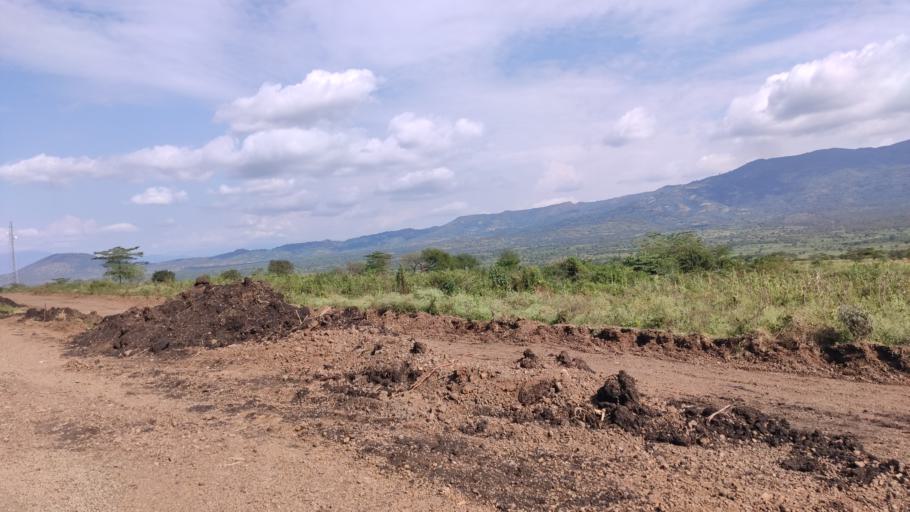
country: ET
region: Southern Nations, Nationalities, and People's Region
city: Felege Neway
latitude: 6.3958
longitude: 37.1066
